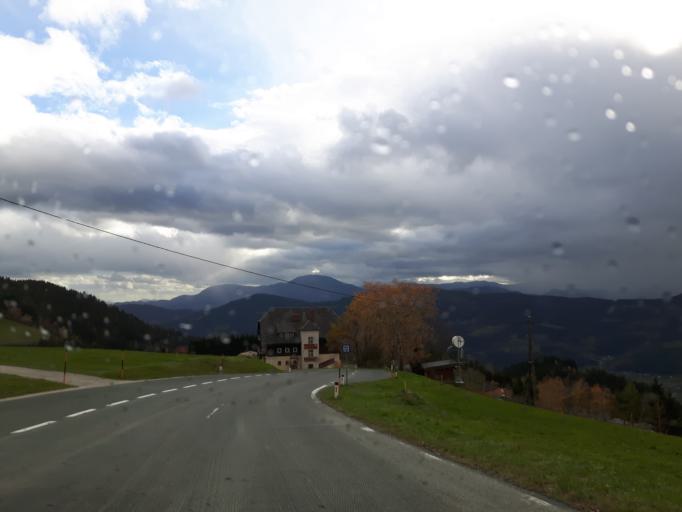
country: AT
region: Carinthia
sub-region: Politischer Bezirk Wolfsberg
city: Lavamund
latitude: 46.6478
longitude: 14.9775
